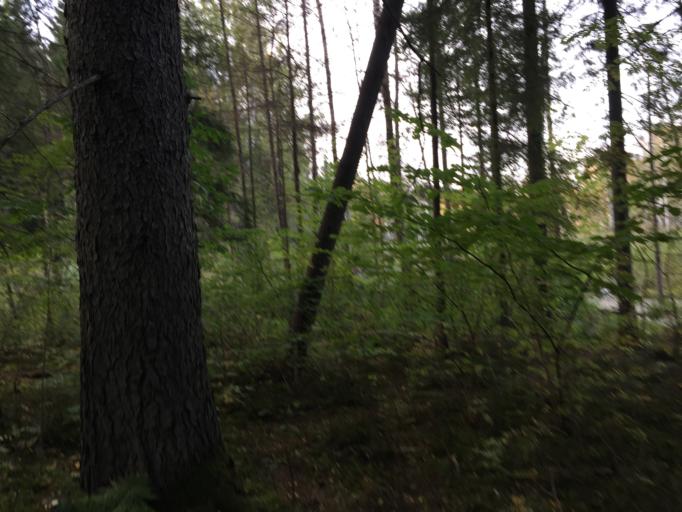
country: LV
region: Baldone
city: Baldone
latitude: 56.7573
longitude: 24.4034
